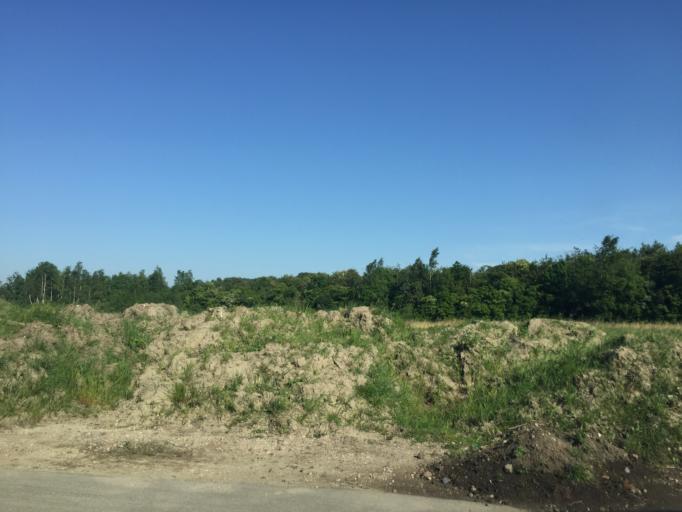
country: DK
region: Capital Region
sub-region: Hvidovre Kommune
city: Hvidovre
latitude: 55.6154
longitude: 12.5177
